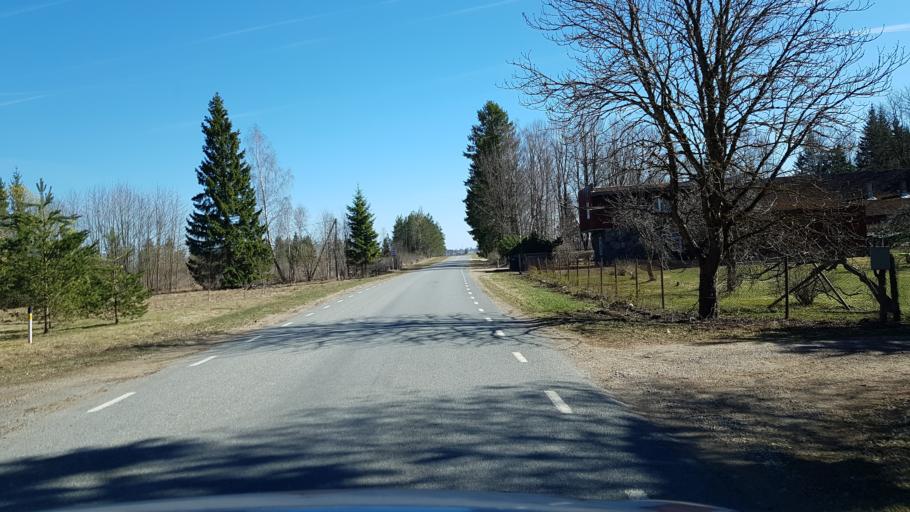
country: EE
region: Laeaene-Virumaa
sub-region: Someru vald
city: Someru
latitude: 59.3612
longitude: 26.4691
